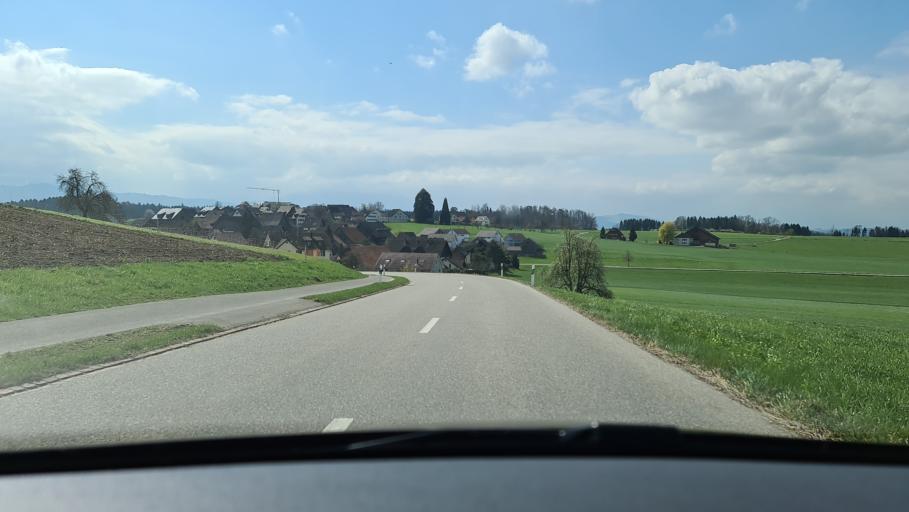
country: CH
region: Zug
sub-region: Zug
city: Steinhausen
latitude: 47.2261
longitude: 8.4973
